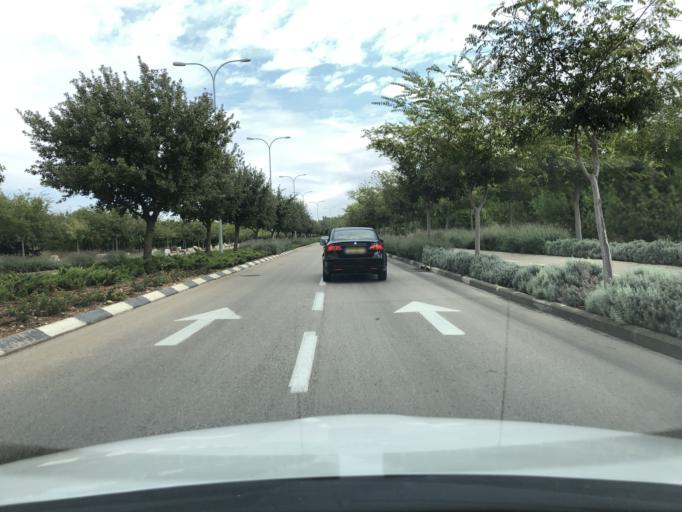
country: PS
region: West Bank
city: Al Midyah
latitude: 31.9210
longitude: 34.9950
